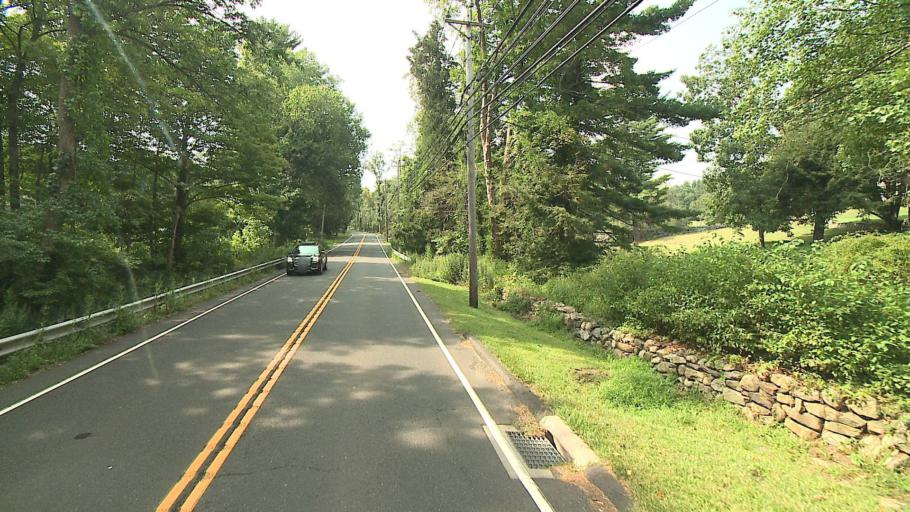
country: US
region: Connecticut
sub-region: Fairfield County
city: Georgetown
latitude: 41.2856
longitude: -73.3997
